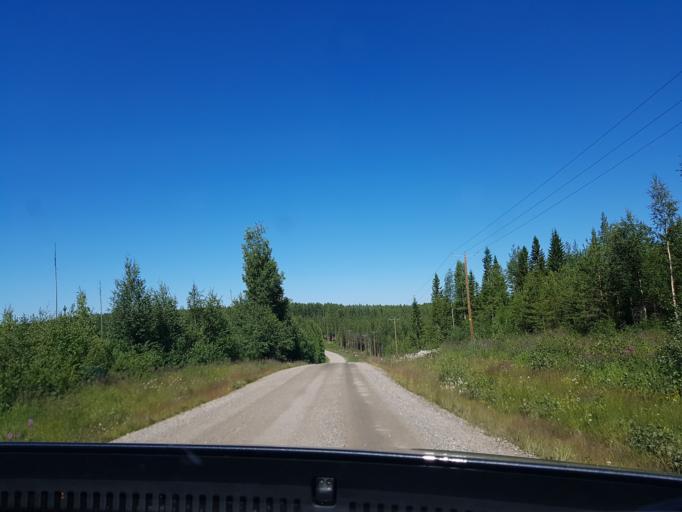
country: FI
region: Kainuu
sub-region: Kehys-Kainuu
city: Kuhmo
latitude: 64.1733
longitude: 29.6364
